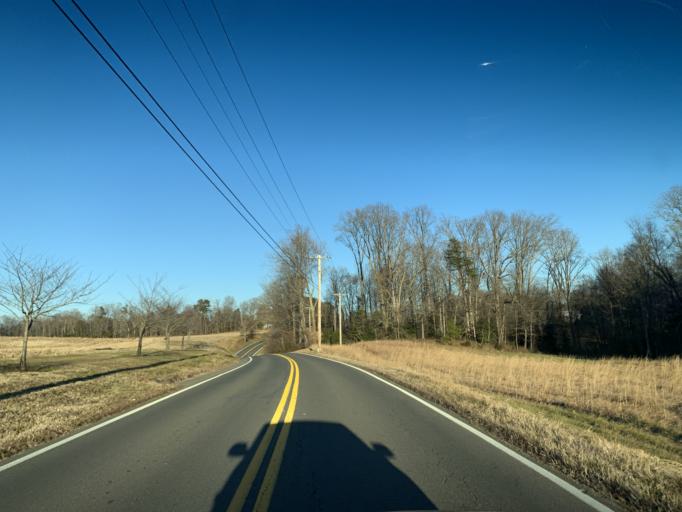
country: US
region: Maryland
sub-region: Saint Mary's County
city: Mechanicsville
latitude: 38.4470
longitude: -76.7228
